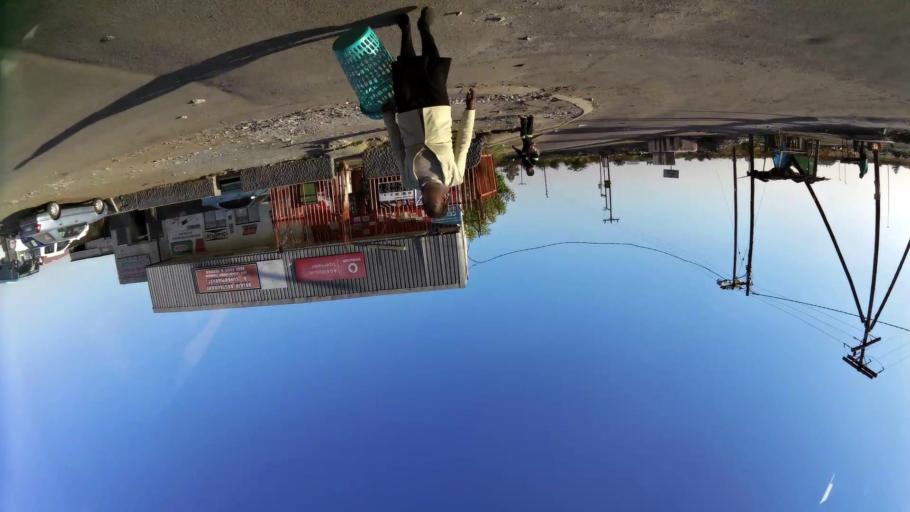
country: ZA
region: North-West
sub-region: Bojanala Platinum District Municipality
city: Rustenburg
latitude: -25.6355
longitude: 27.2199
